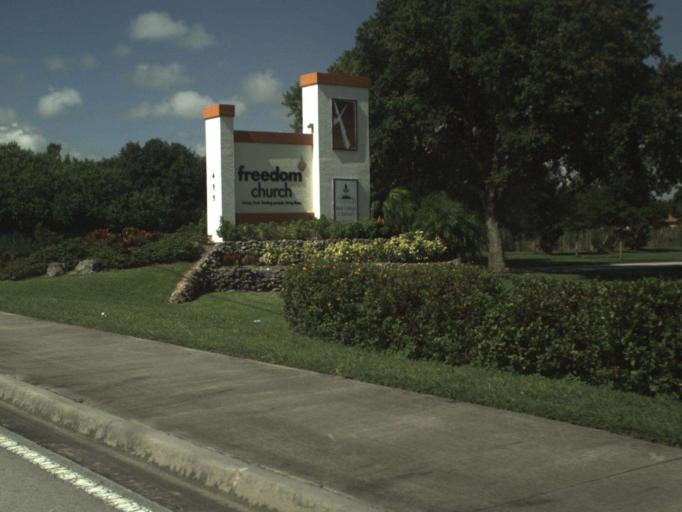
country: US
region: Florida
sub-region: Indian River County
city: Vero Beach South
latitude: 27.5970
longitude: -80.4474
